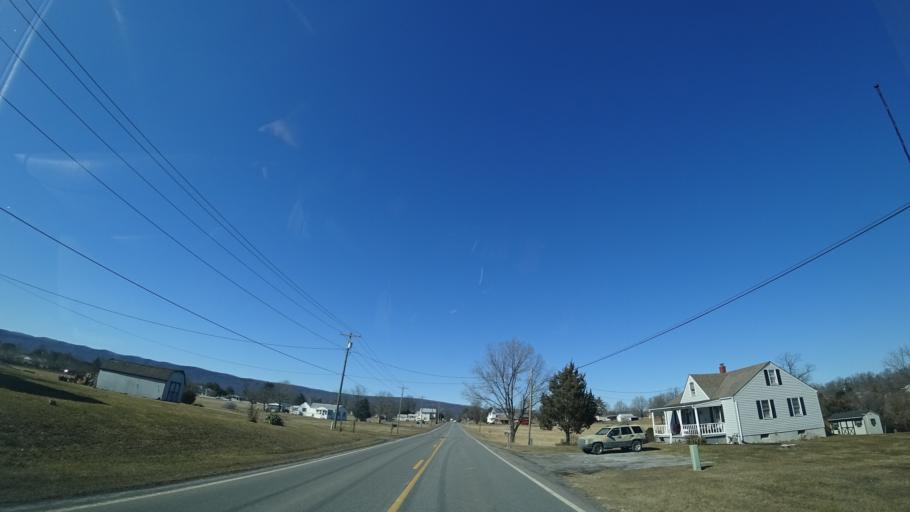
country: US
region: Virginia
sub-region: Shenandoah County
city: Strasburg
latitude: 39.0231
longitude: -78.3626
